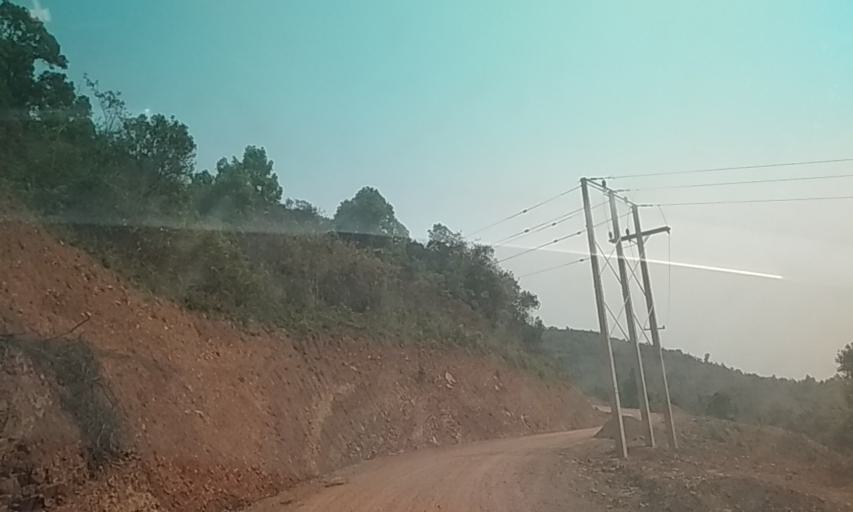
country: VN
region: Huyen Dien Bien
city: Dien Bien Phu
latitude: 21.4744
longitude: 102.7742
